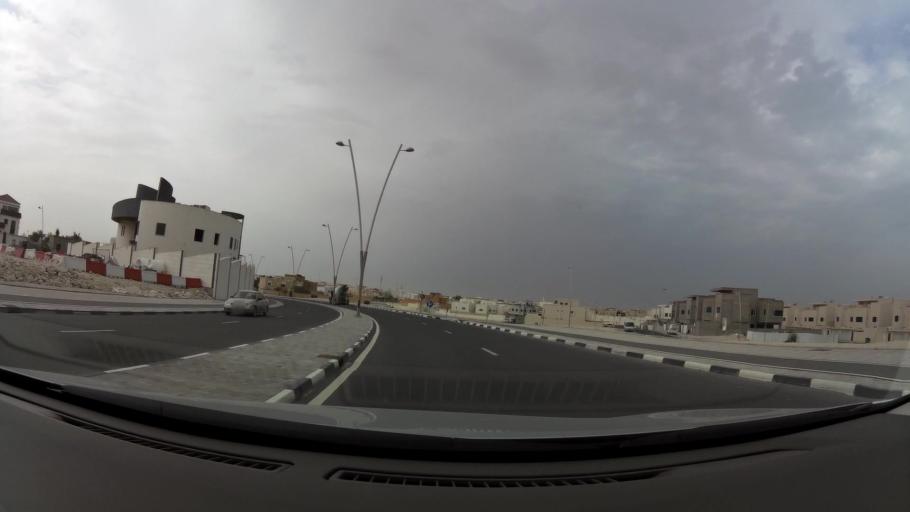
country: QA
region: Baladiyat ad Dawhah
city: Doha
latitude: 25.3421
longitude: 51.4944
